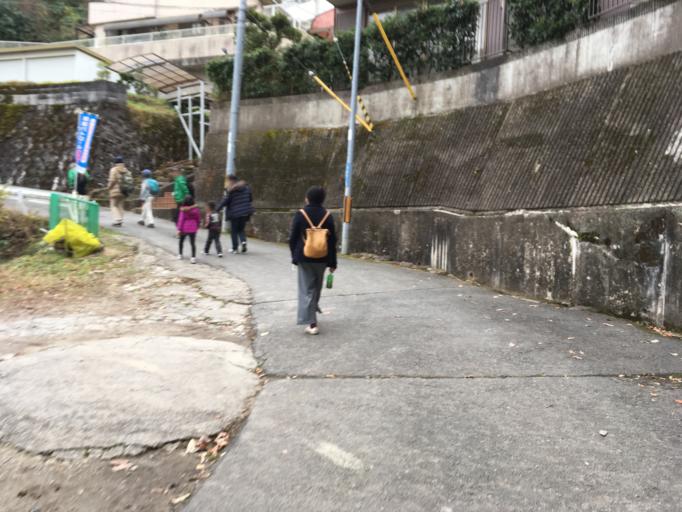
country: JP
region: Nara
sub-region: Ikoma-shi
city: Ikoma
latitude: 34.6888
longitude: 135.6862
